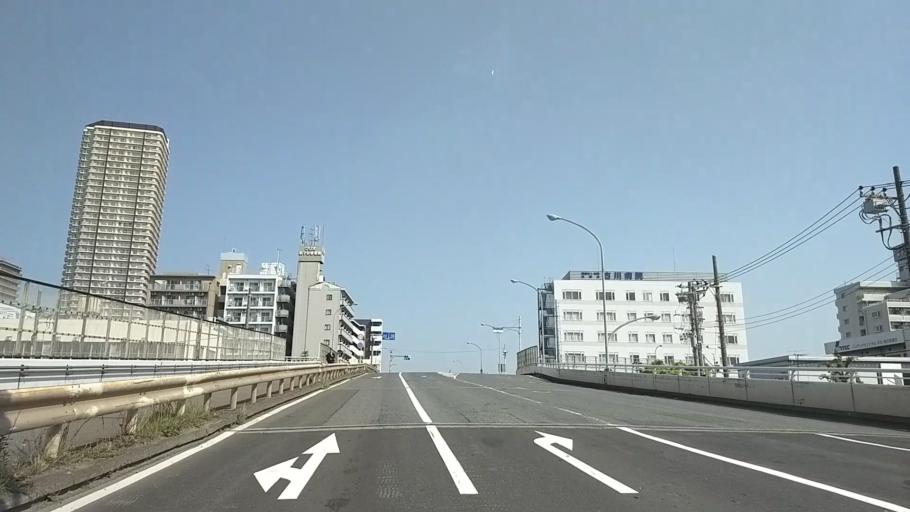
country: JP
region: Kanagawa
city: Yokohama
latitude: 35.4846
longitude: 139.6557
